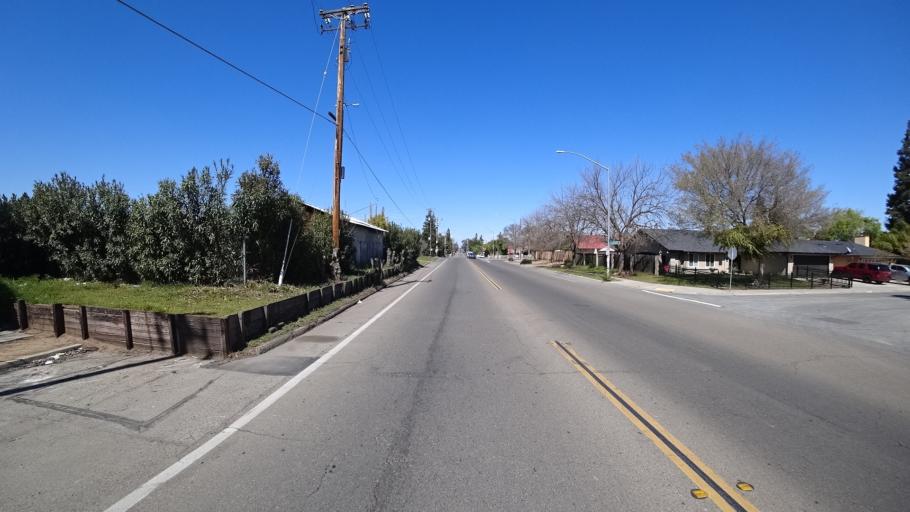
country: US
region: California
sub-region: Fresno County
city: West Park
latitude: 36.7854
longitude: -119.8624
